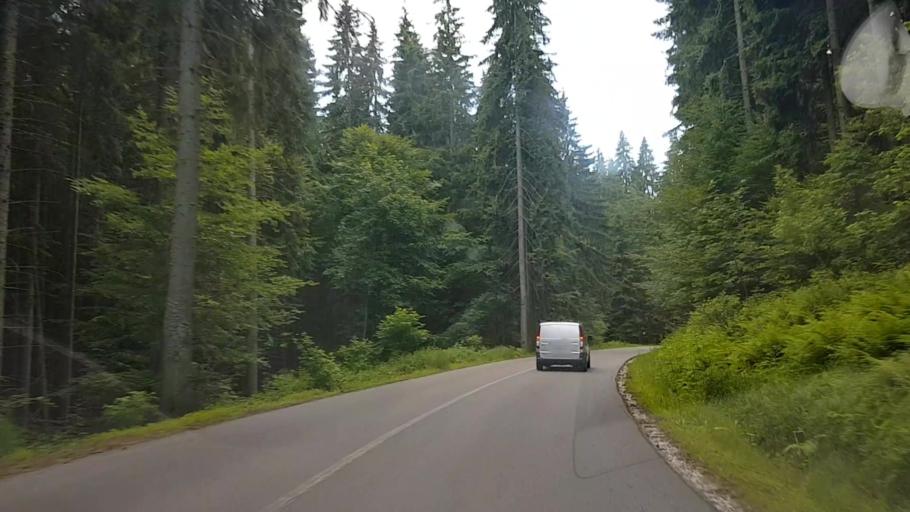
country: RO
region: Harghita
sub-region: Comuna Varsag
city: Varsag
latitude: 46.6696
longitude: 25.3256
